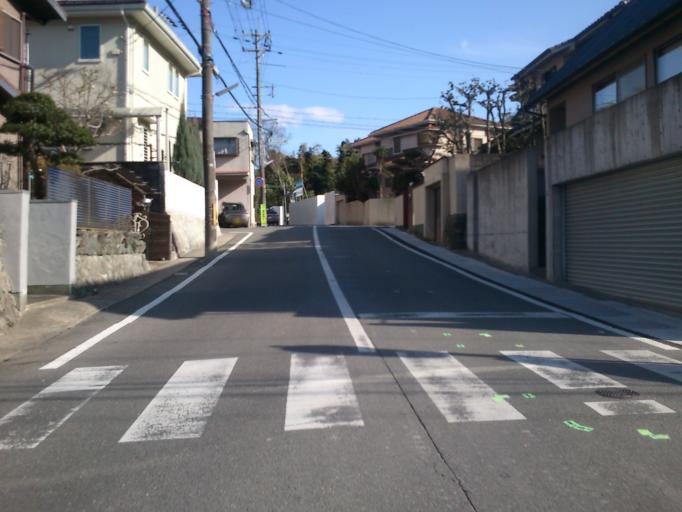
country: JP
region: Kyoto
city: Yawata
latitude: 34.9142
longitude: 135.6767
